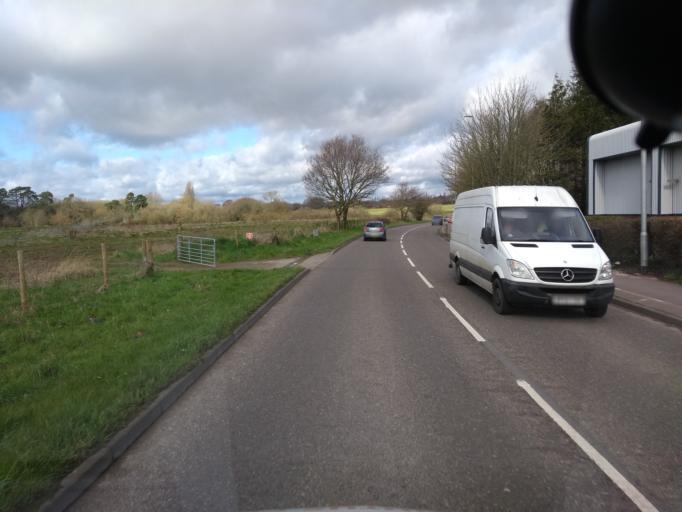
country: GB
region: England
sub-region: Somerset
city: Yeovil
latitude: 50.9344
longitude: -2.6672
